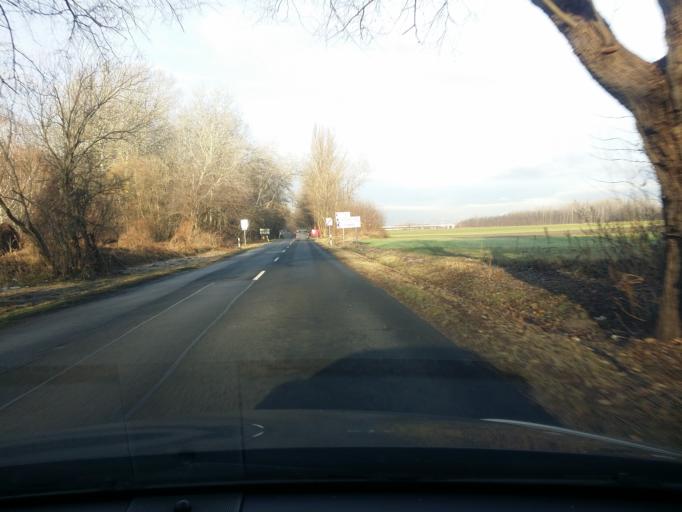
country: HU
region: Pest
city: Alsonemedi
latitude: 47.3371
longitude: 19.1331
